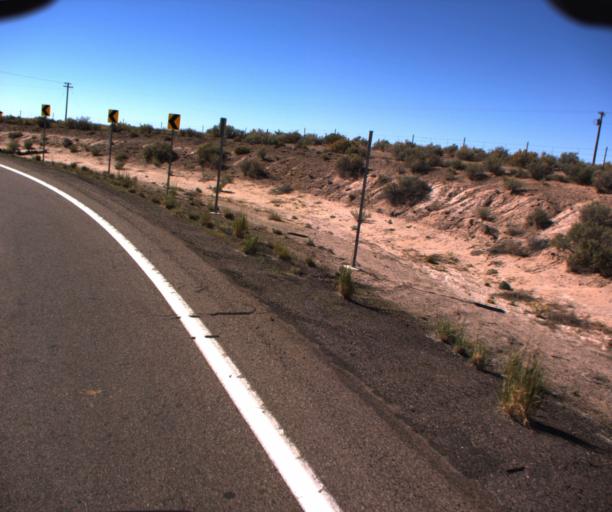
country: US
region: Arizona
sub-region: Navajo County
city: Holbrook
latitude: 34.9392
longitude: -110.1309
